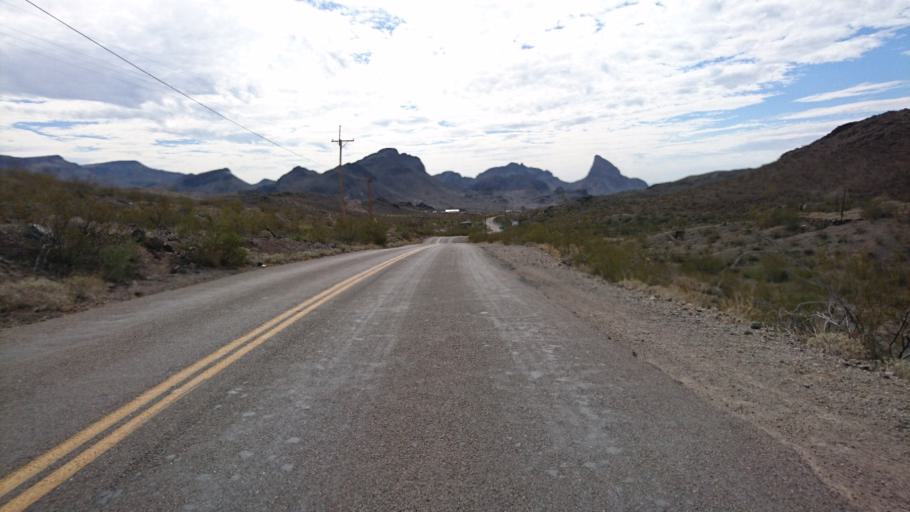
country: US
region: Arizona
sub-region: Mohave County
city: Bullhead City
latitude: 35.0218
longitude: -114.3829
